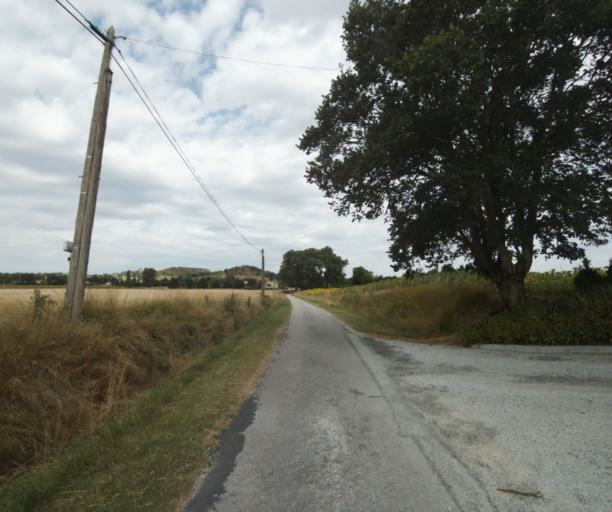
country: FR
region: Midi-Pyrenees
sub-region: Departement de la Haute-Garonne
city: Saint-Felix-Lauragais
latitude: 43.4401
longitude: 1.9113
